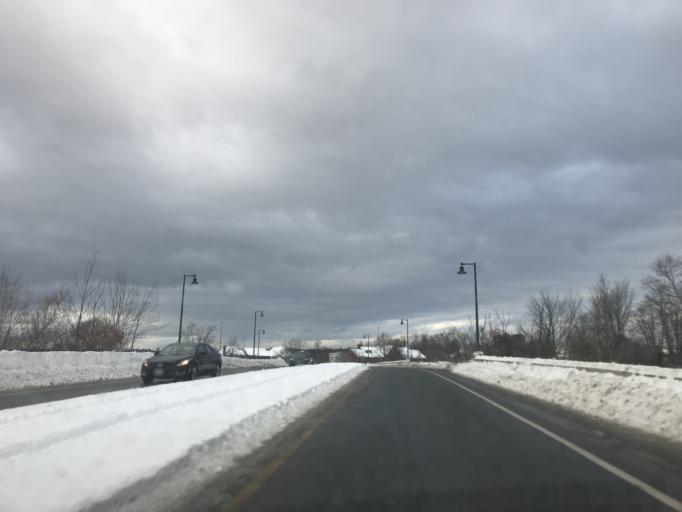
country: US
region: Maine
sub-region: Cumberland County
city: Portland
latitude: 43.6501
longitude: -70.2841
